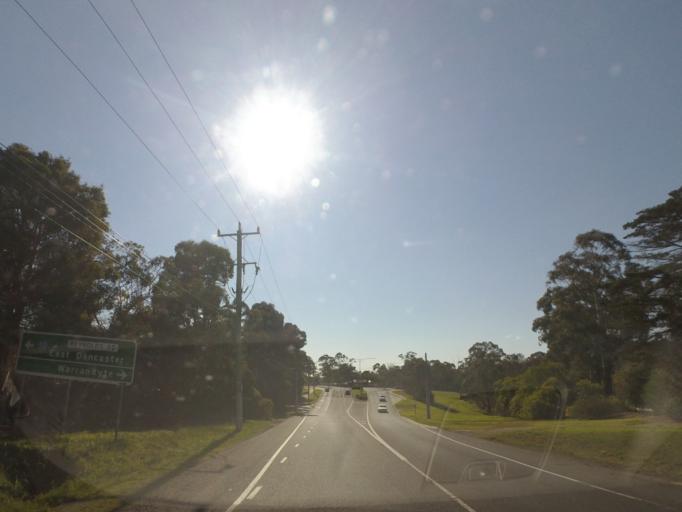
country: AU
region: Victoria
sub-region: Manningham
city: Donvale
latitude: -37.7671
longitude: 145.1828
